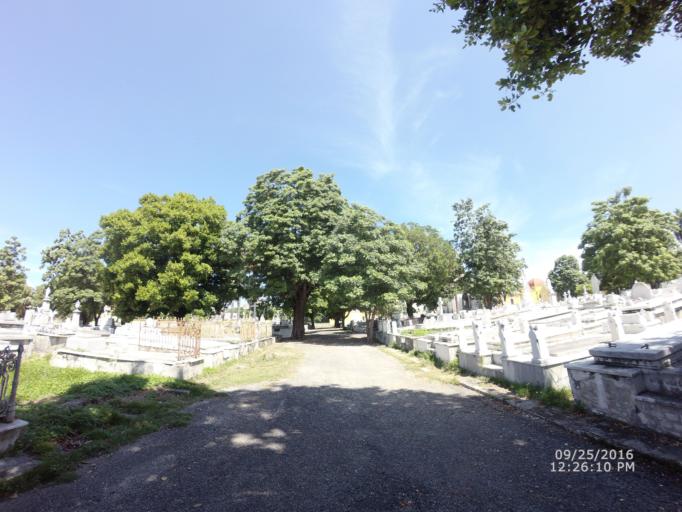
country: CU
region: La Habana
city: Havana
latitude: 23.1251
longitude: -82.3973
